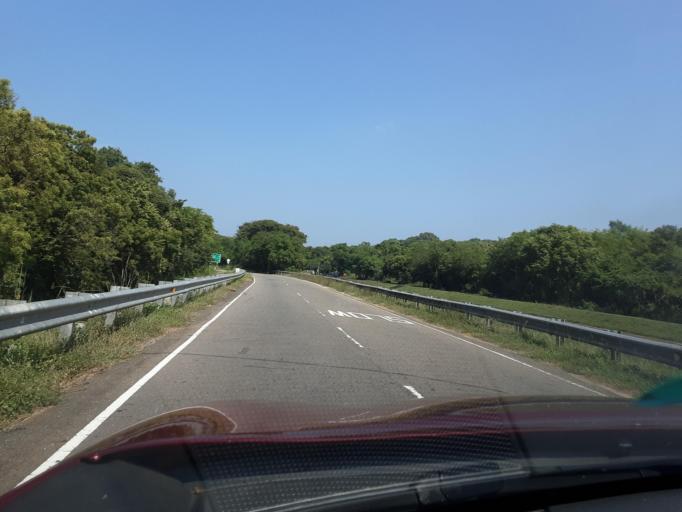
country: LK
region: Uva
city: Badulla
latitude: 7.2812
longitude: 81.0442
